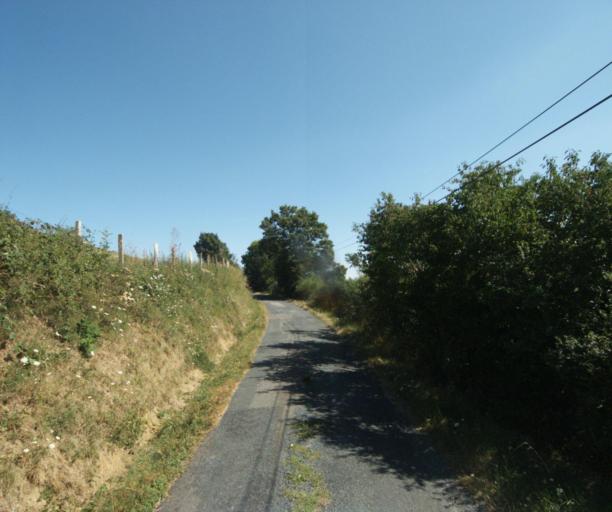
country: FR
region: Rhone-Alpes
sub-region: Departement du Rhone
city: Montrottier
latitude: 45.8127
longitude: 4.4908
